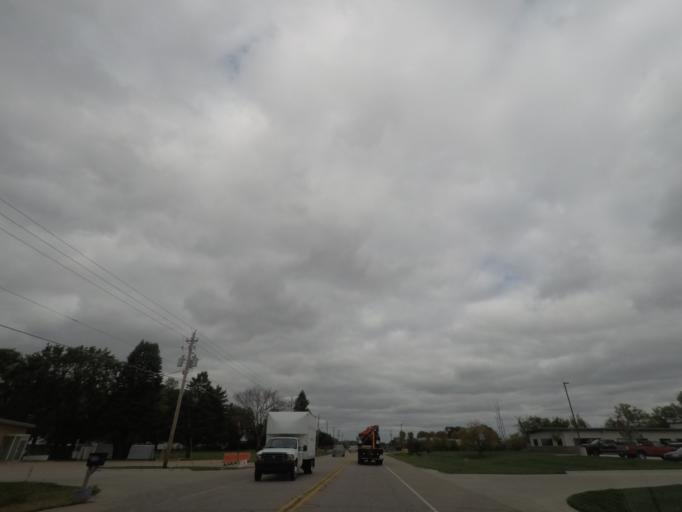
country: US
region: Iowa
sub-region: Polk County
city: Saylorville
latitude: 41.6763
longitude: -93.6006
